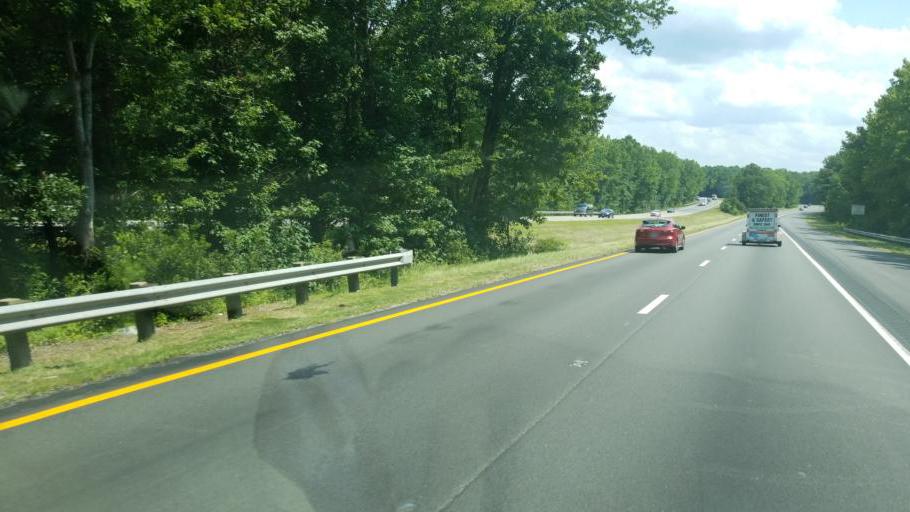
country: US
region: Virginia
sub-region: City of Suffolk
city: Suffolk
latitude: 36.7589
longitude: -76.5337
